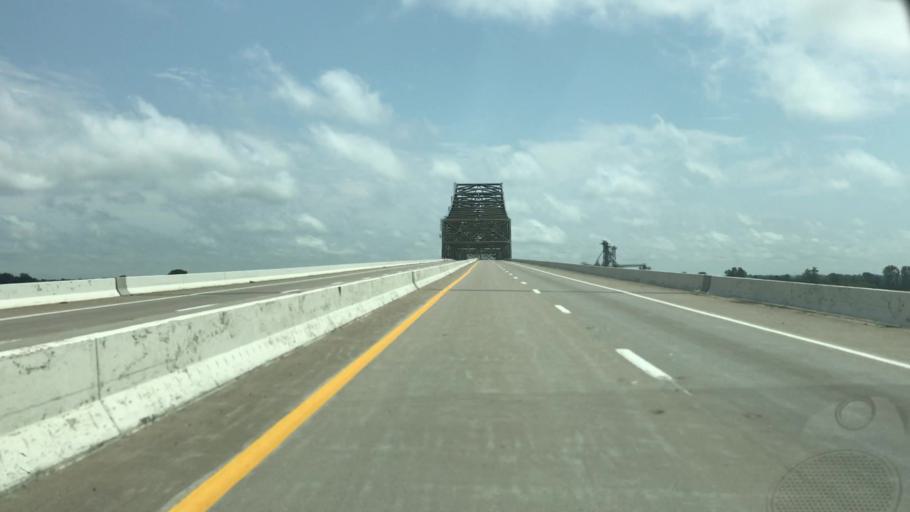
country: US
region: Missouri
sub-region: Pemiscot County
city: Caruthersville
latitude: 36.1181
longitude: -89.6149
